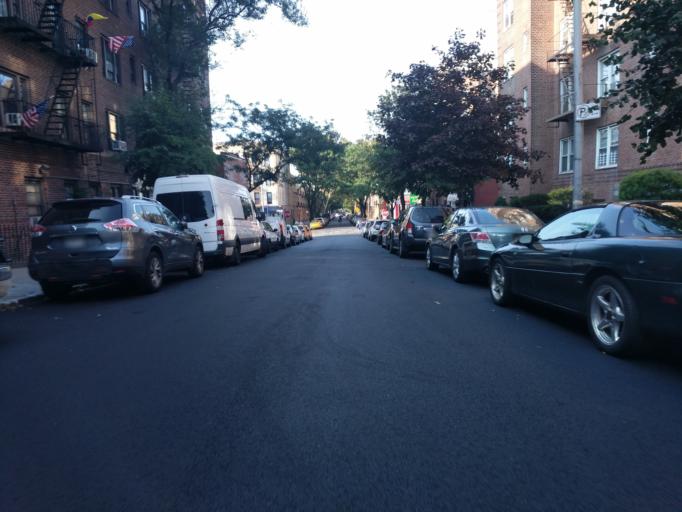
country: US
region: New York
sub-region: Queens County
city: Long Island City
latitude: 40.7437
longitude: -73.9158
